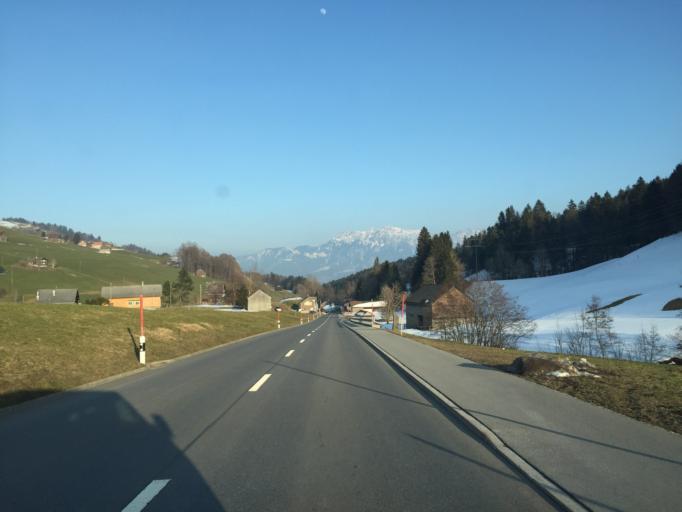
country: CH
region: Saint Gallen
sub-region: Wahlkreis Toggenburg
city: Wildhaus
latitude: 47.1994
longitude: 9.3649
